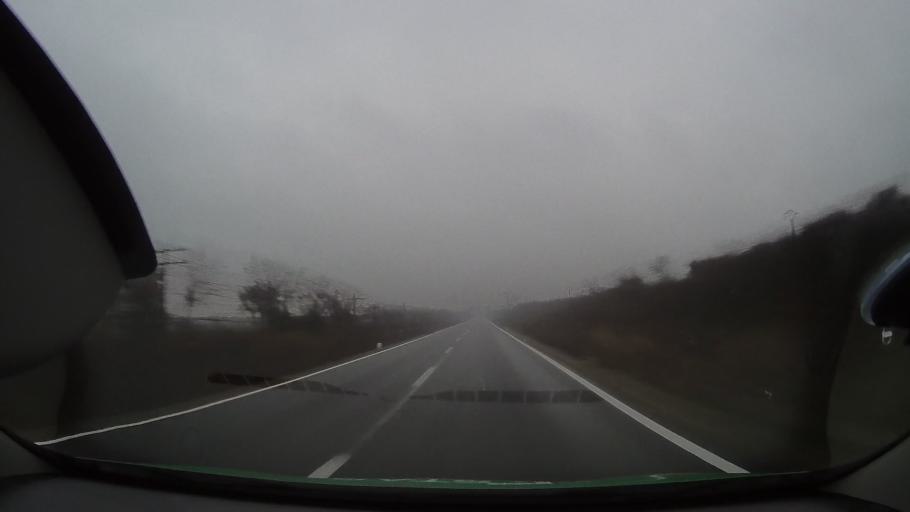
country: RO
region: Bihor
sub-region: Comuna Olcea
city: Calacea
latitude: 46.7224
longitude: 21.9487
